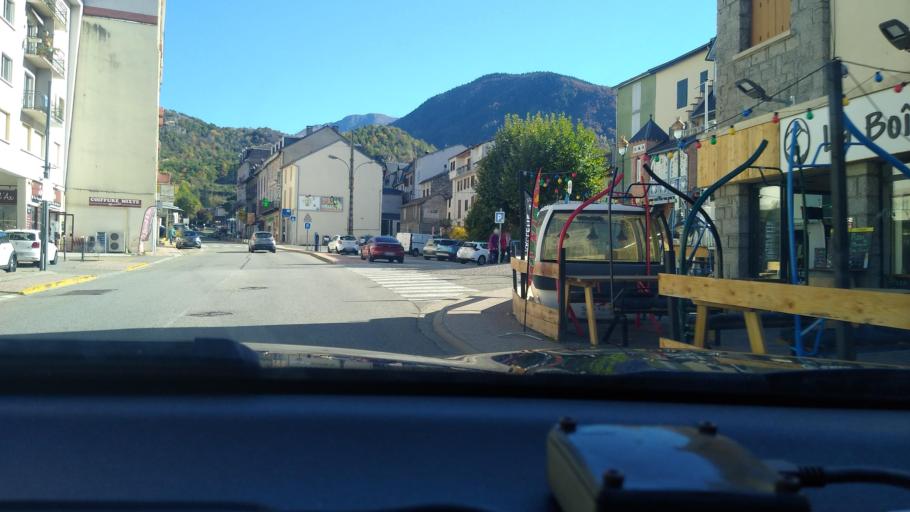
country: FR
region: Midi-Pyrenees
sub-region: Departement de l'Ariege
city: Ax-les-Thermes
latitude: 42.7217
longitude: 1.8374
